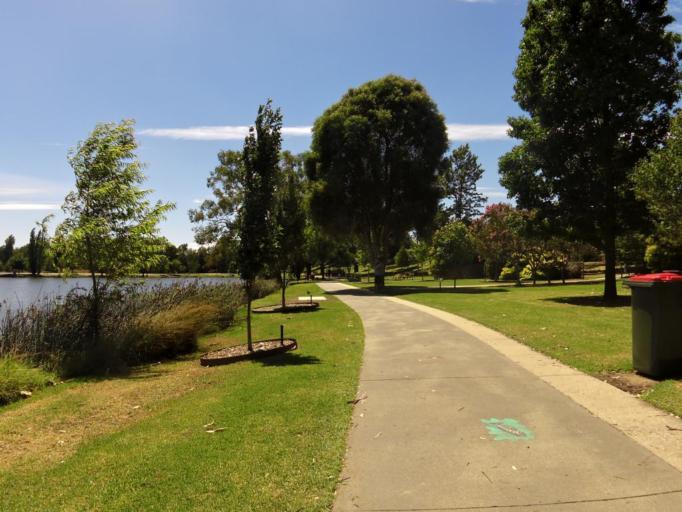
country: AU
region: Victoria
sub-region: Wodonga
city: Wodonga
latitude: -36.1136
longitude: 146.8902
